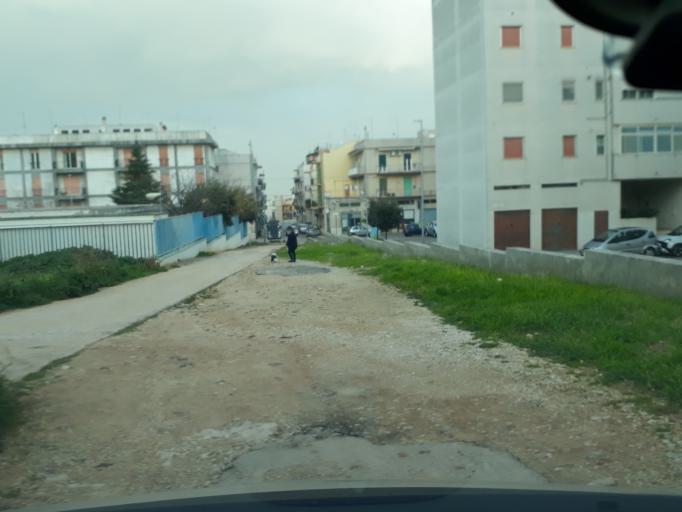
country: IT
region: Apulia
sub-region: Provincia di Brindisi
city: Fasano
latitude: 40.8369
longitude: 17.3530
